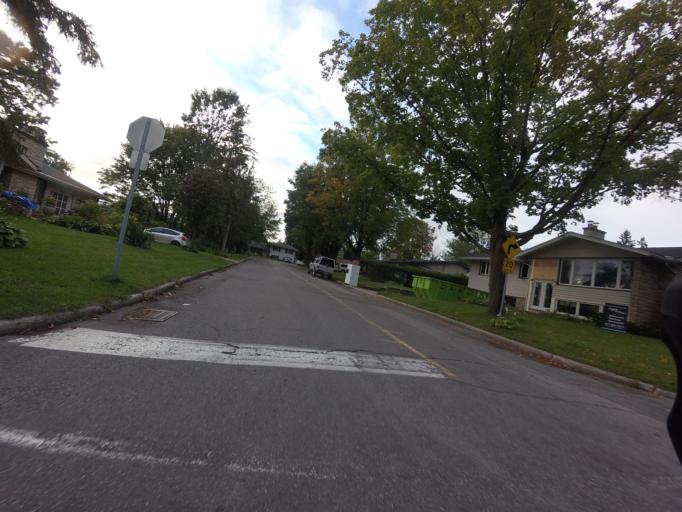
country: CA
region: Ontario
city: Ottawa
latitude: 45.3644
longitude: -75.7593
